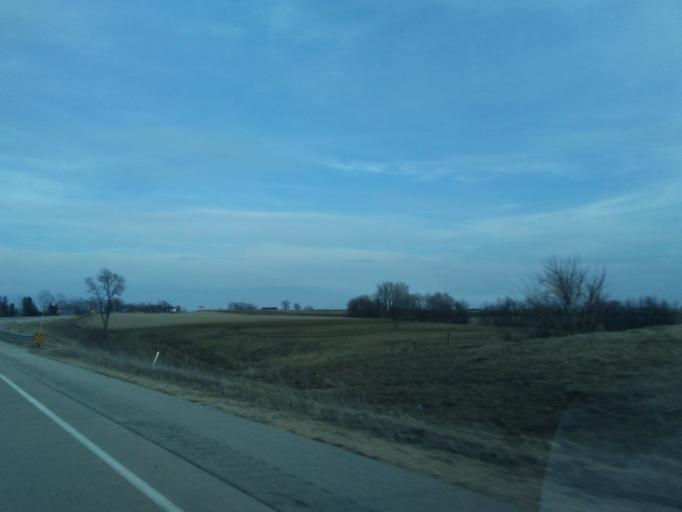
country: US
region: Wisconsin
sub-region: Dane County
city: Mount Horeb
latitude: 43.0102
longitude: -89.7977
